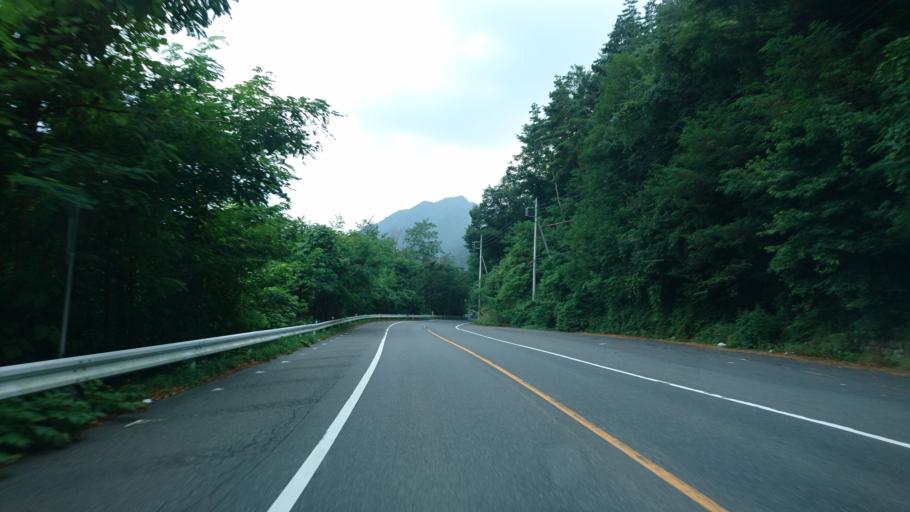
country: JP
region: Gunma
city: Numata
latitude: 36.7190
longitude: 139.2139
